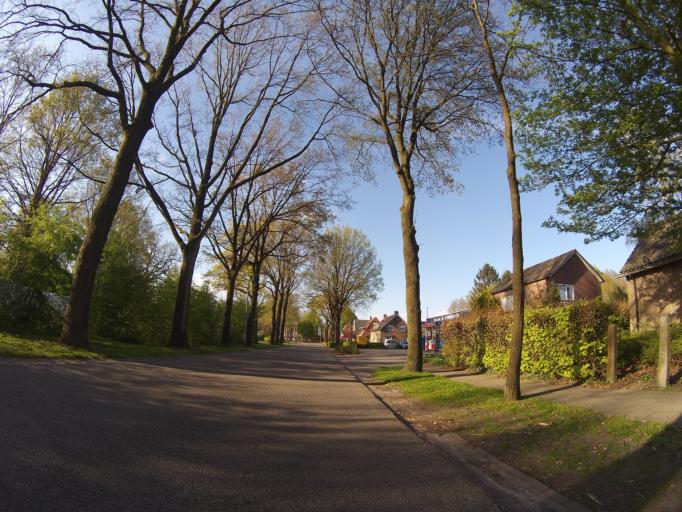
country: NL
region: Drenthe
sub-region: Gemeente Coevorden
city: Dalen
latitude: 52.7538
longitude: 6.7189
